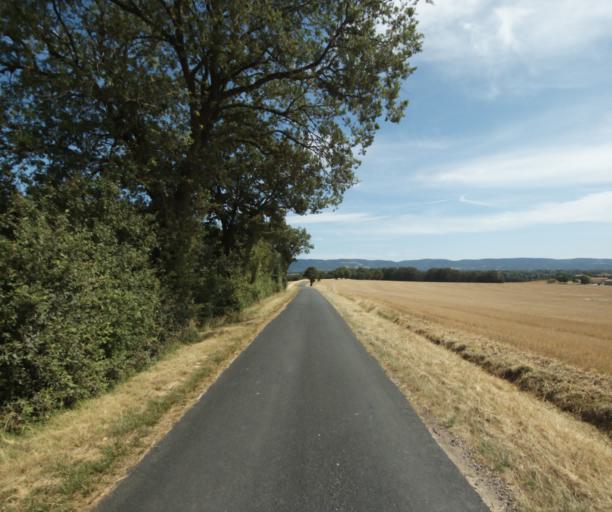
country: FR
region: Midi-Pyrenees
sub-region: Departement du Tarn
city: Puylaurens
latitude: 43.5312
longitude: 2.0201
